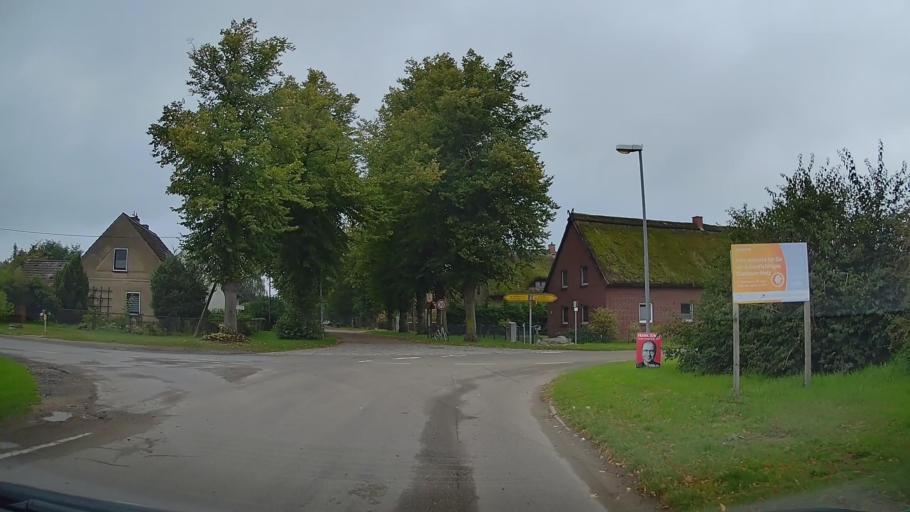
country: DE
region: Mecklenburg-Vorpommern
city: Blowatz
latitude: 53.9634
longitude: 11.5467
